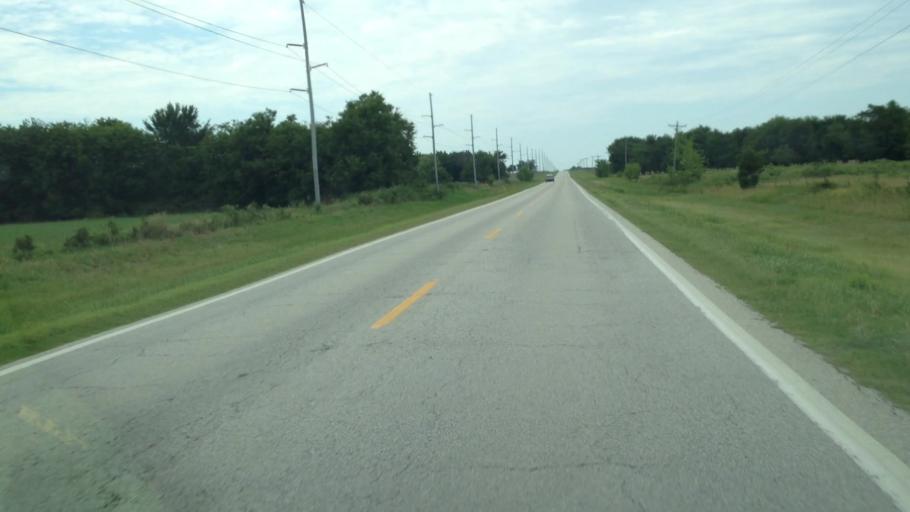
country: US
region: Kansas
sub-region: Labette County
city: Chetopa
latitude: 36.9082
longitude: -95.0896
